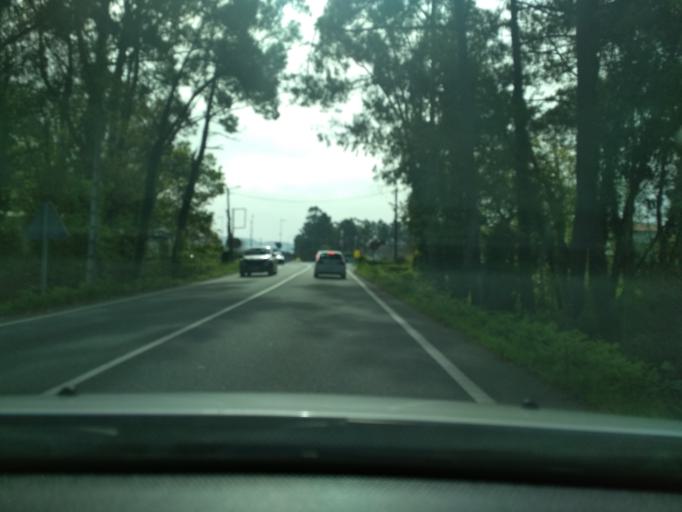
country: ES
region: Galicia
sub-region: Provincia de Pontevedra
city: Catoira
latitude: 42.6721
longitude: -8.7112
